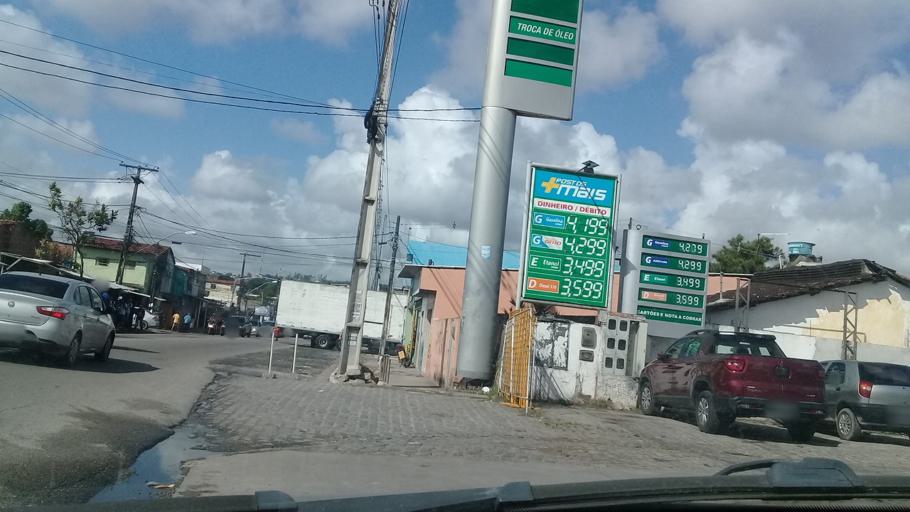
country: BR
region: Pernambuco
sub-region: Recife
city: Recife
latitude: -8.1092
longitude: -34.9355
